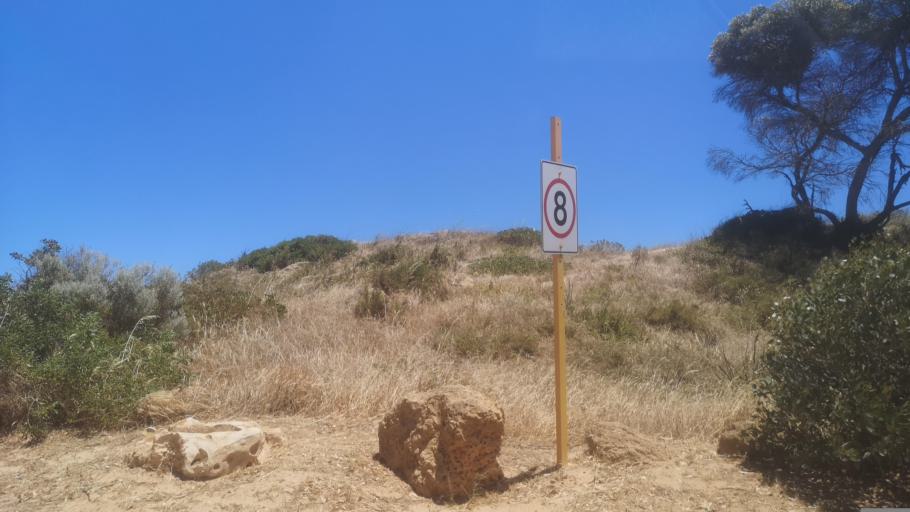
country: AU
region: Western Australia
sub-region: Dandaragan
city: Jurien Bay
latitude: -30.1838
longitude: 114.9984
